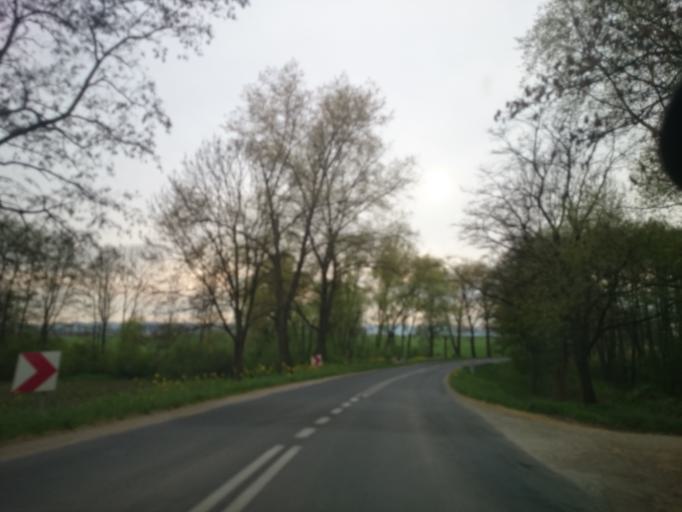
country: PL
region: Lower Silesian Voivodeship
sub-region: Powiat zabkowicki
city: Zabkowice Slaskie
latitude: 50.5823
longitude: 16.8558
